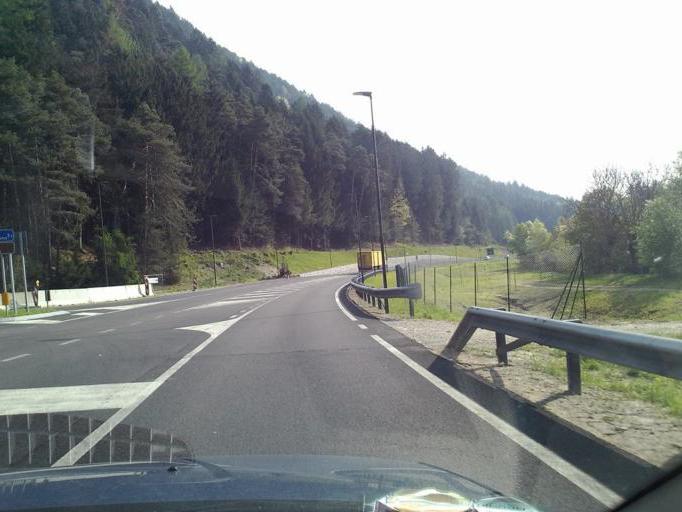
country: IT
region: Trentino-Alto Adige
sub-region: Bolzano
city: Terento
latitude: 46.8115
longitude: 11.7769
